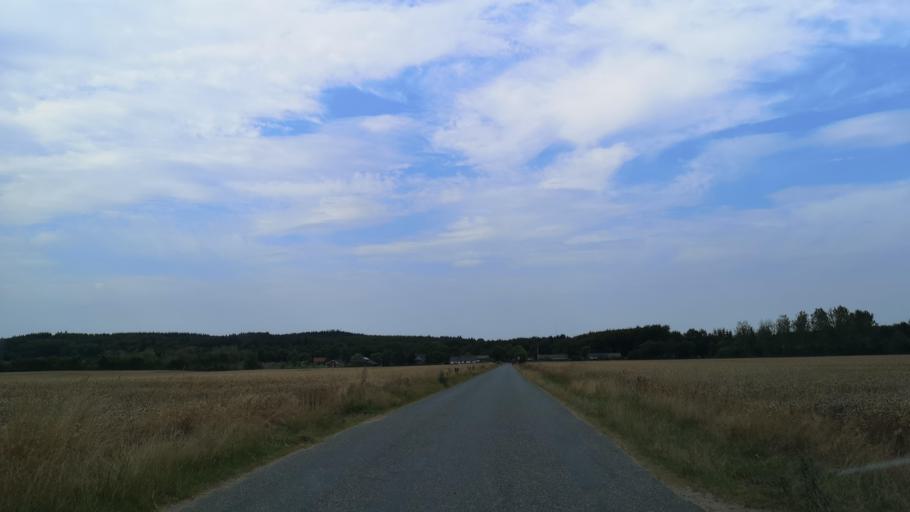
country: DK
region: Central Jutland
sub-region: Ringkobing-Skjern Kommune
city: Videbaek
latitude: 56.0496
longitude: 8.6903
